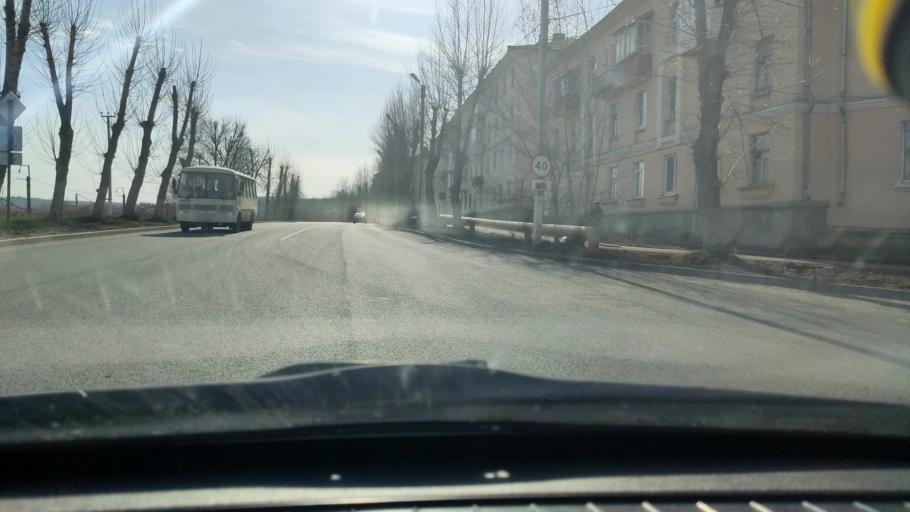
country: RU
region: Samara
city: Zhigulevsk
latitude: 53.4048
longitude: 49.4948
